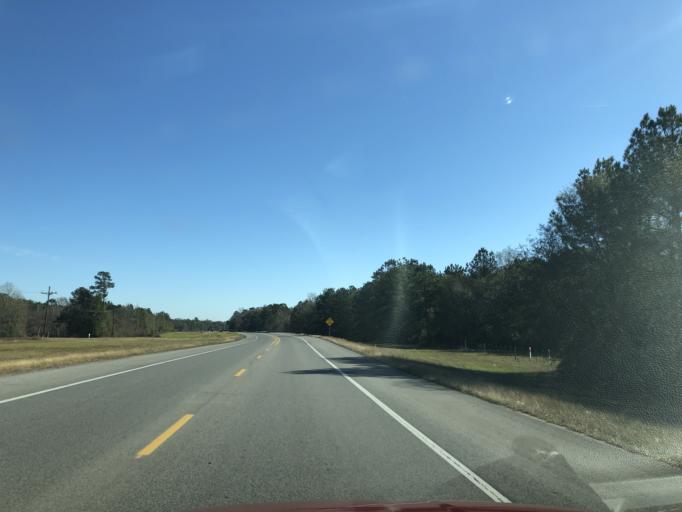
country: US
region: Texas
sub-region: Montgomery County
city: Porter Heights
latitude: 30.2138
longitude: -95.3123
